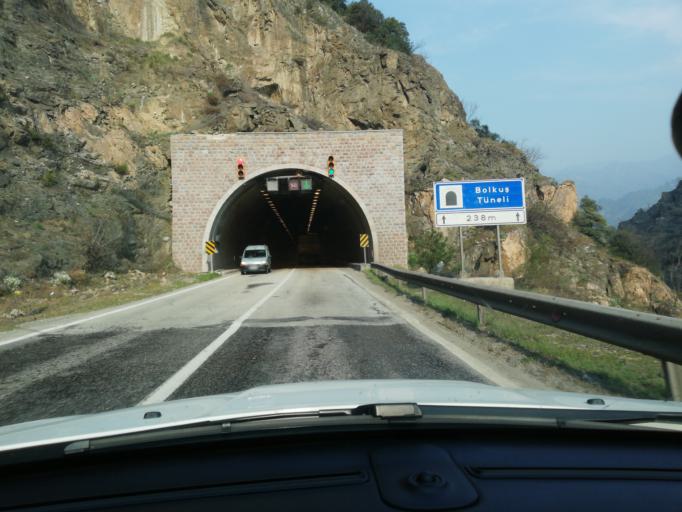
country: TR
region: Karabuk
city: Karabuk
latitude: 41.1533
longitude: 32.5224
